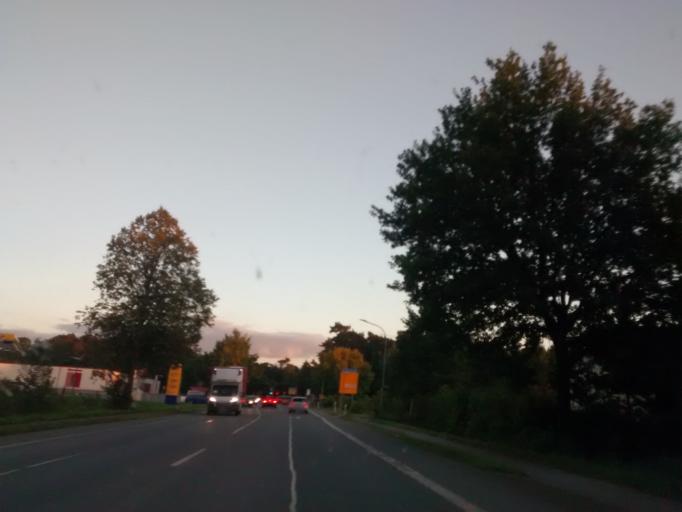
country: DE
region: North Rhine-Westphalia
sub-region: Regierungsbezirk Detmold
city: Steinhagen
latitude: 52.0333
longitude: 8.3975
